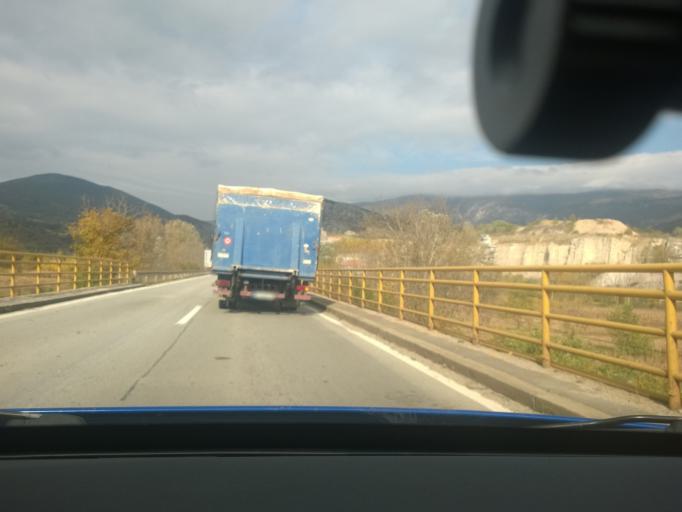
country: RS
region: Central Serbia
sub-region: Nisavski Okrug
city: Svrljig
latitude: 43.3006
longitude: 22.1971
